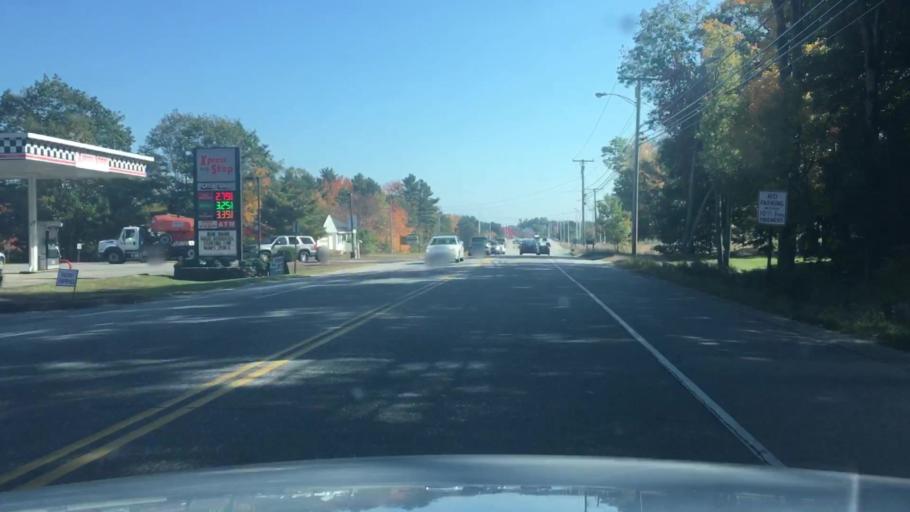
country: US
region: Maine
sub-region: Sagadahoc County
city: Topsham
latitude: 43.9449
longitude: -69.9838
